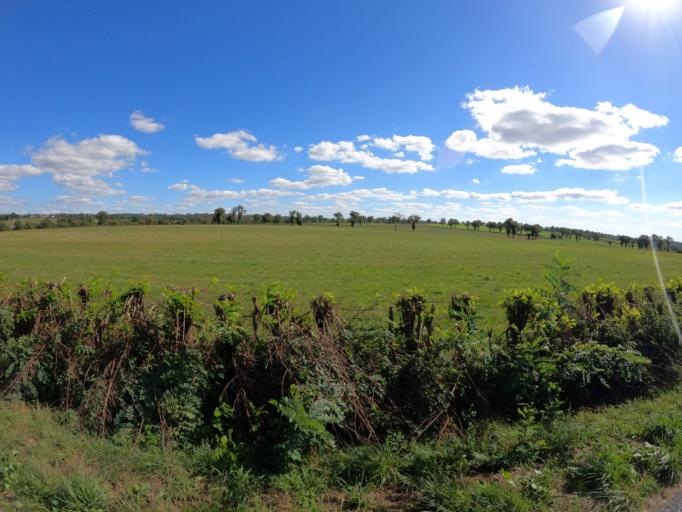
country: FR
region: Auvergne
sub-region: Departement de l'Allier
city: Doyet
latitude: 46.3946
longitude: 2.8288
